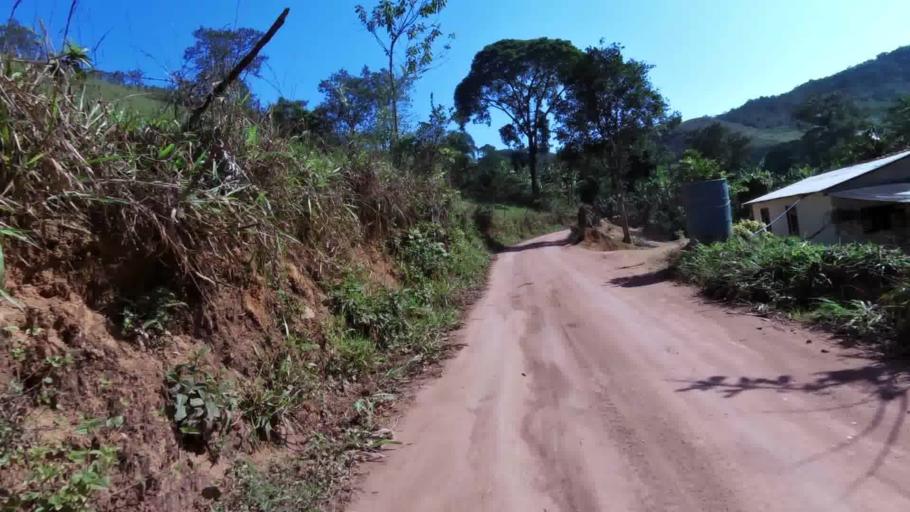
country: BR
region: Espirito Santo
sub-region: Alfredo Chaves
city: Alfredo Chaves
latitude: -20.5630
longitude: -40.7715
